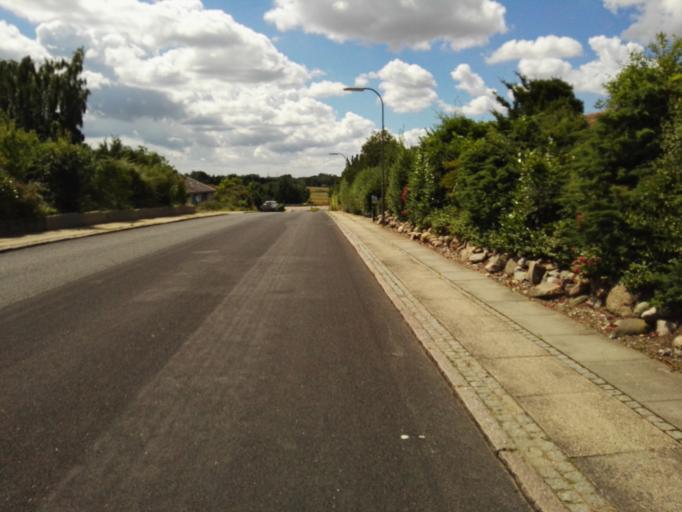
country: DK
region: Capital Region
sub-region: Ballerup Kommune
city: Ballerup
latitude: 55.7499
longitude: 12.3483
